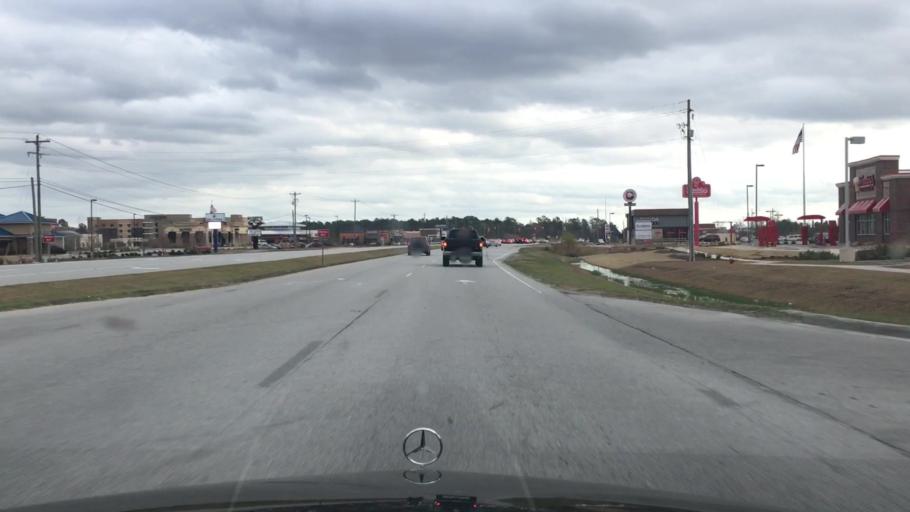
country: US
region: North Carolina
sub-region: Onslow County
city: Pumpkin Center
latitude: 34.7985
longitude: -77.4142
